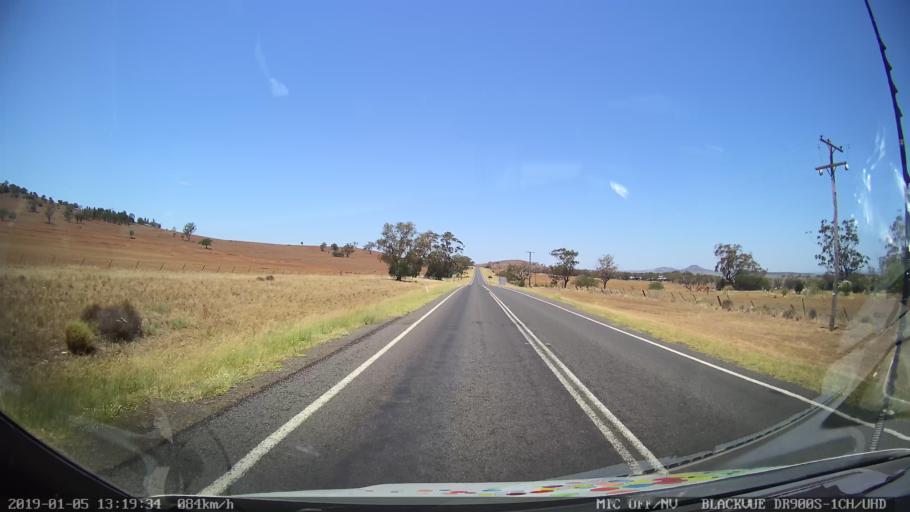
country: AU
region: New South Wales
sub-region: Gunnedah
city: Gunnedah
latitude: -31.0977
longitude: 149.9221
